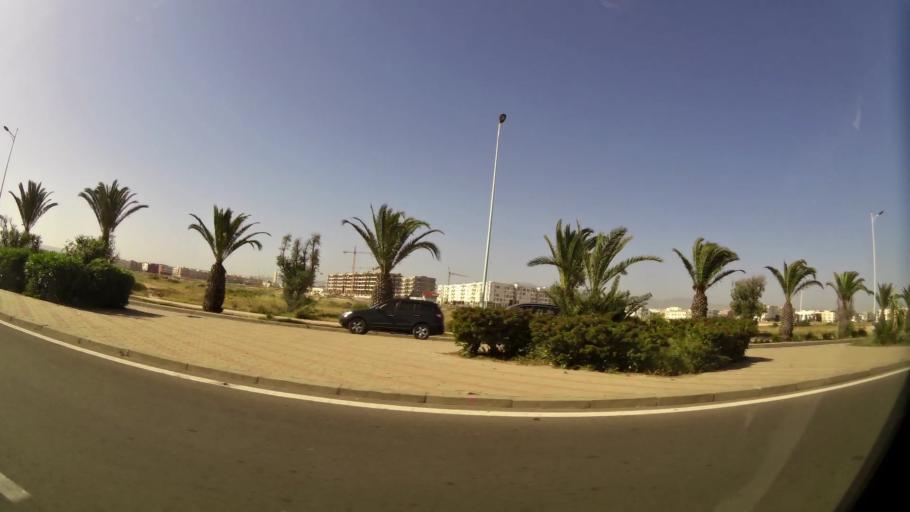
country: MA
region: Oued ed Dahab-Lagouira
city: Dakhla
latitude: 30.4031
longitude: -9.5668
